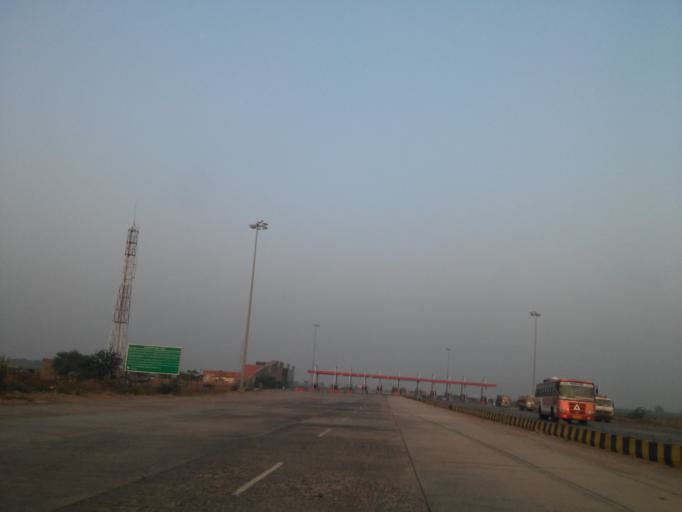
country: IN
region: Gujarat
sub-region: Rajkot
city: Morbi
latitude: 23.0366
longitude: 70.9304
